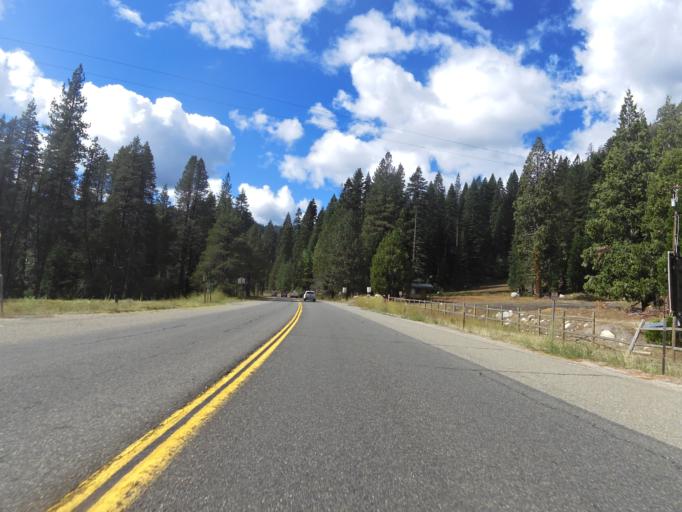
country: US
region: California
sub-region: El Dorado County
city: South Lake Tahoe
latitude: 38.7947
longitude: -120.1492
